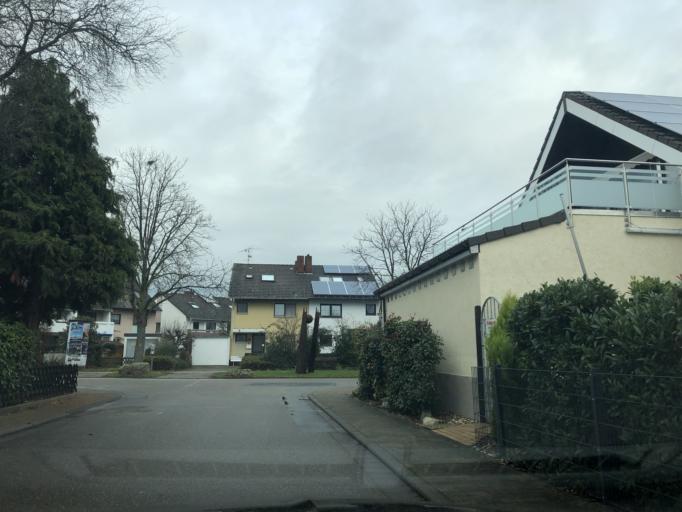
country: DE
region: Baden-Wuerttemberg
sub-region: Karlsruhe Region
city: Eppelheim
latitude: 49.4009
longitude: 8.6209
